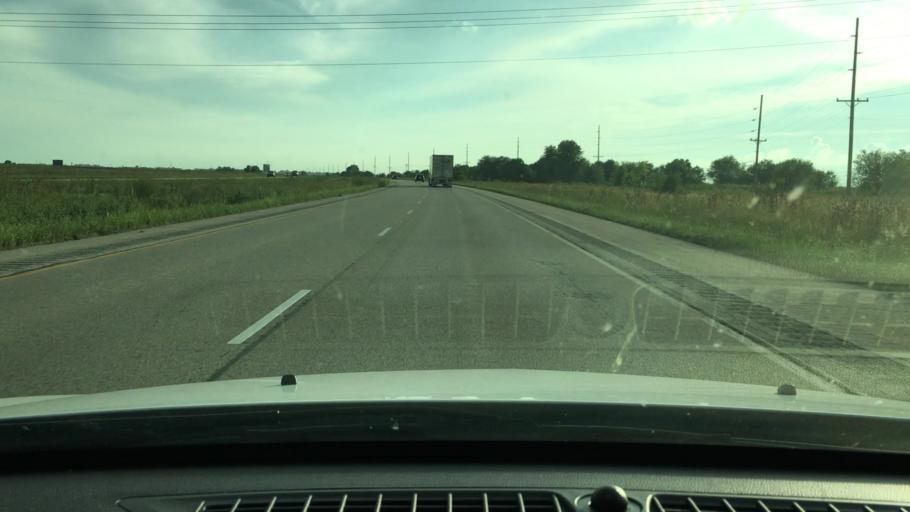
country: US
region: Illinois
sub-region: Logan County
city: Atlanta
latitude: 40.3033
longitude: -89.1811
